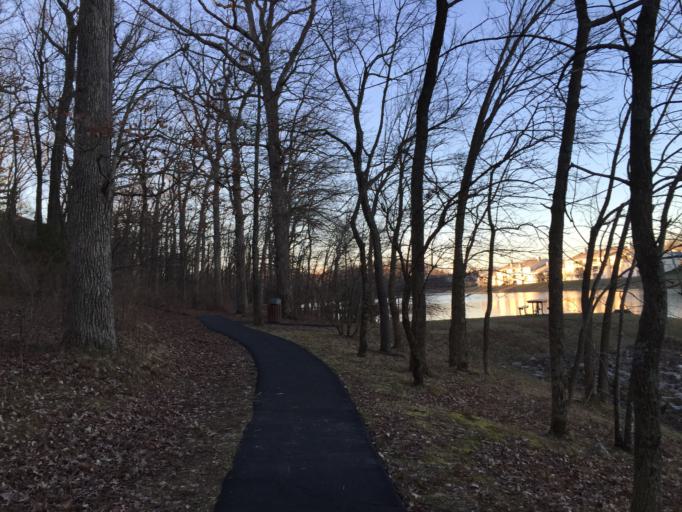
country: US
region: Missouri
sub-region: Saint Louis County
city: Ellisville
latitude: 38.5815
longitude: -90.6093
